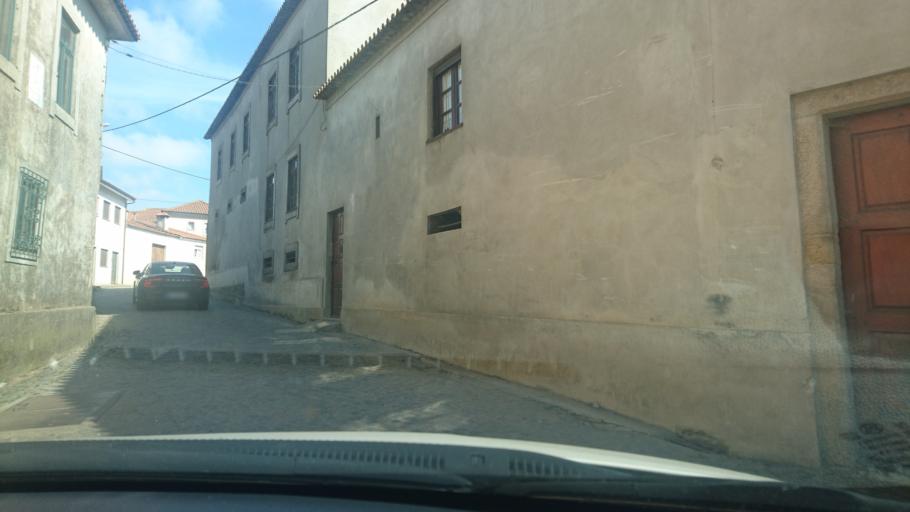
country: PT
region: Porto
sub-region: Matosinhos
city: Lavra
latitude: 41.2674
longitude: -8.7114
